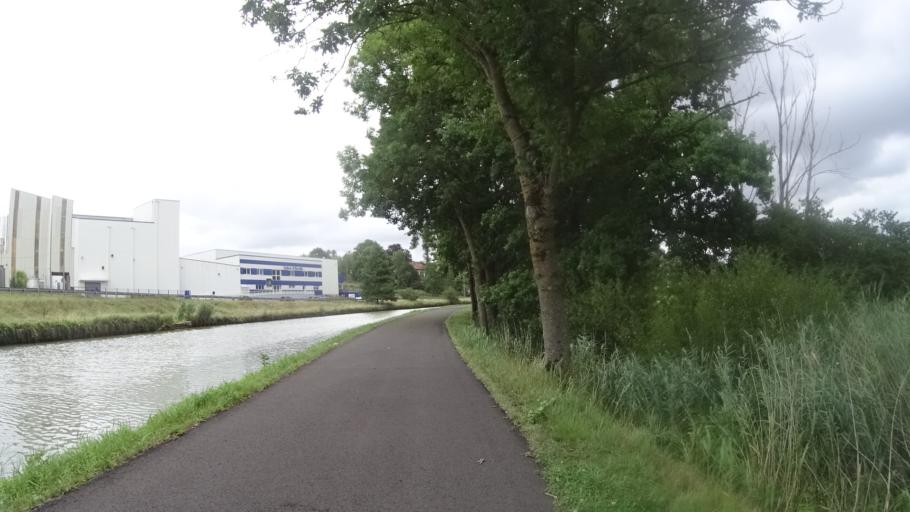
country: FR
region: Lorraine
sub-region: Departement de Meurthe-et-Moselle
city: Einville-au-Jard
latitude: 48.6523
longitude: 6.4653
